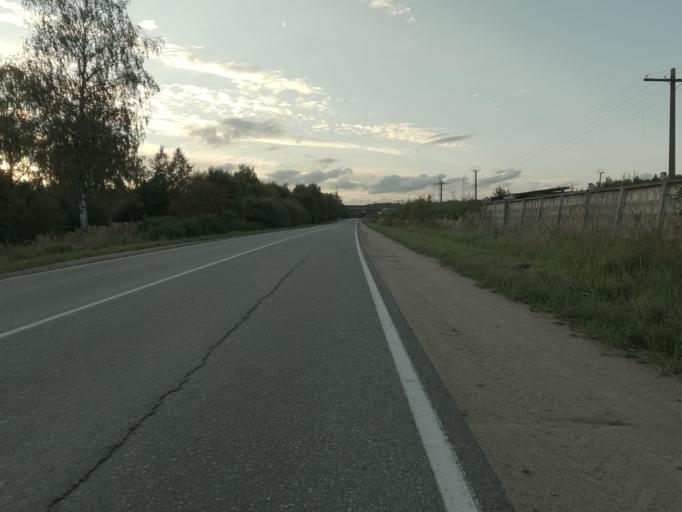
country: RU
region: Leningrad
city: Mga
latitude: 59.7551
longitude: 31.0234
